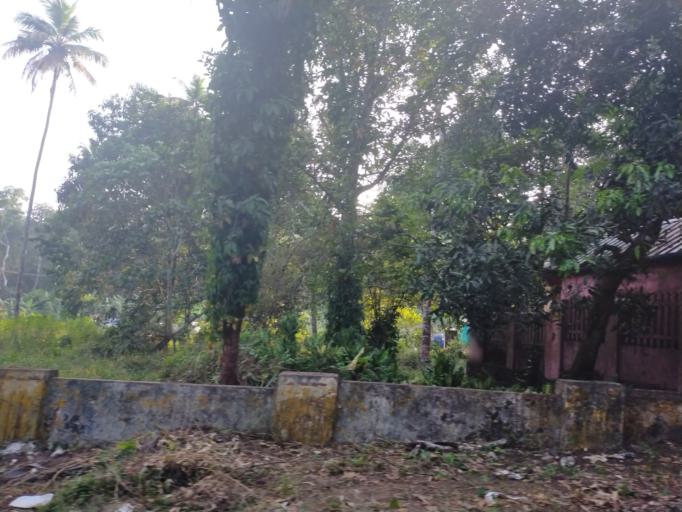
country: IN
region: Kerala
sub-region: Kottayam
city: Vaikam
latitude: 9.7472
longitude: 76.5118
